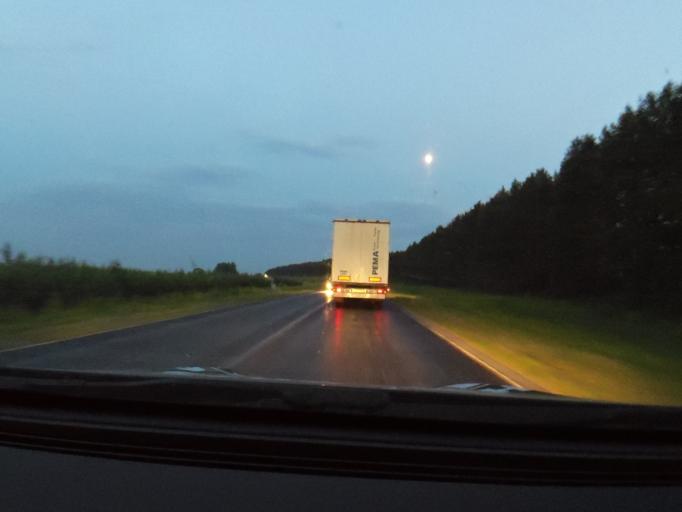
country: RU
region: Bashkortostan
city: Duvan
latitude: 56.0584
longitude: 58.1915
